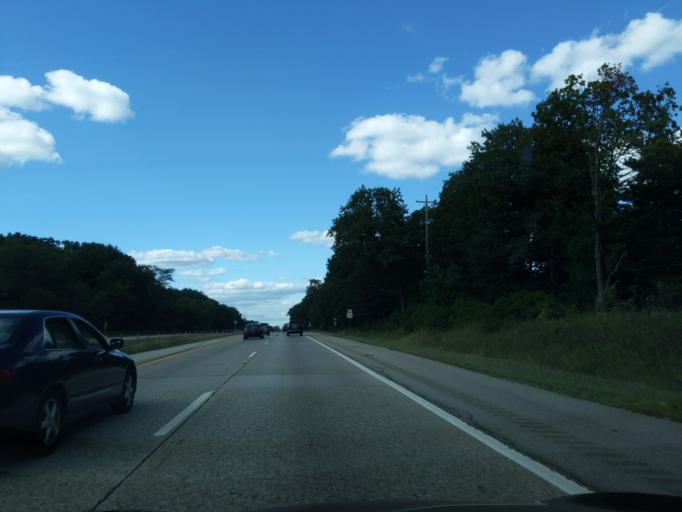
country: US
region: Michigan
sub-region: Muskegon County
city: Muskegon Heights
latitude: 43.1799
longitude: -86.2050
